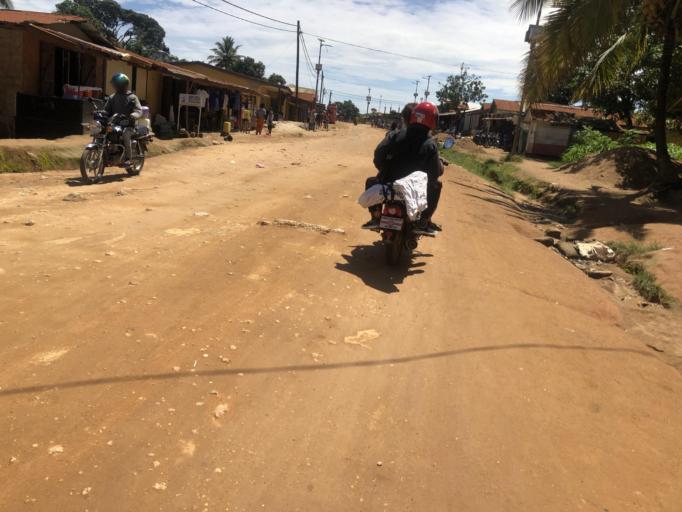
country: SL
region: Eastern Province
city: Koidu
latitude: 8.6390
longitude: -10.9576
